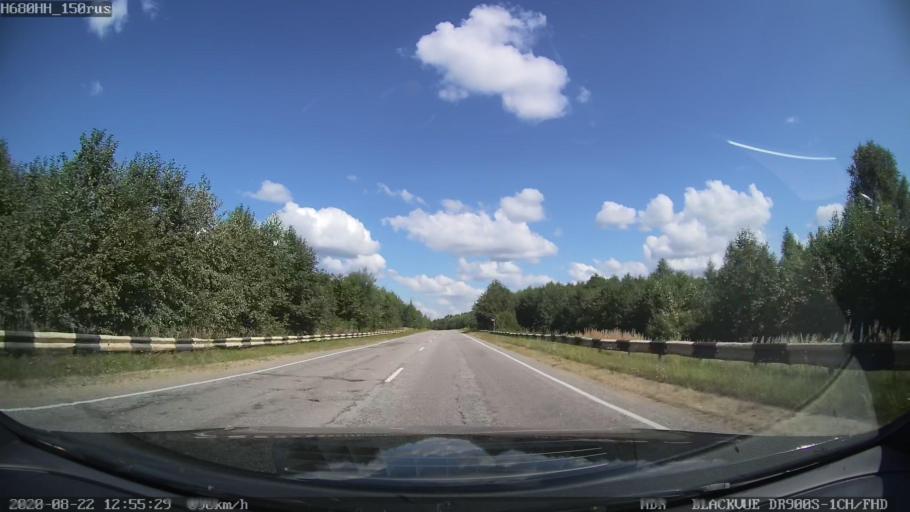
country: RU
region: Tverskaya
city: Rameshki
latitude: 57.5442
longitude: 36.3025
